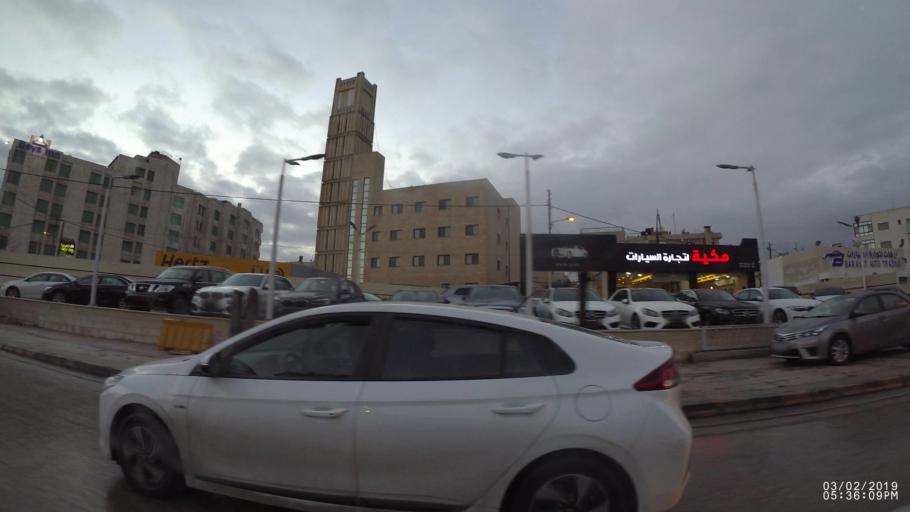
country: JO
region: Amman
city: Al Jubayhah
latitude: 31.9767
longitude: 35.8880
